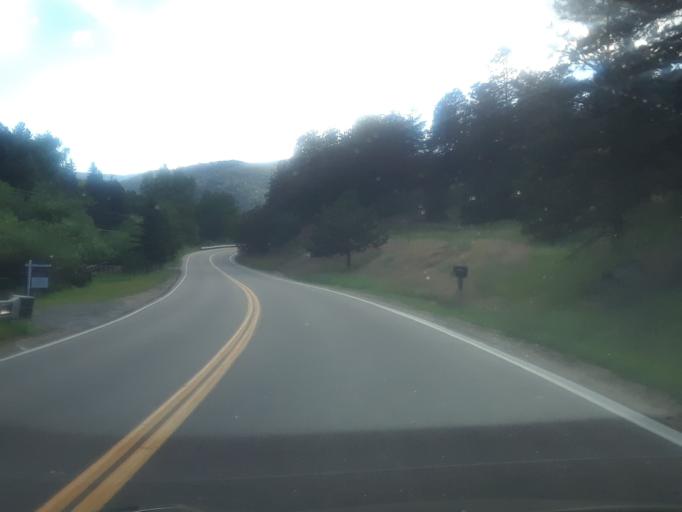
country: US
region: Colorado
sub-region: Jefferson County
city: Kittredge
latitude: 39.7171
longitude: -105.3813
